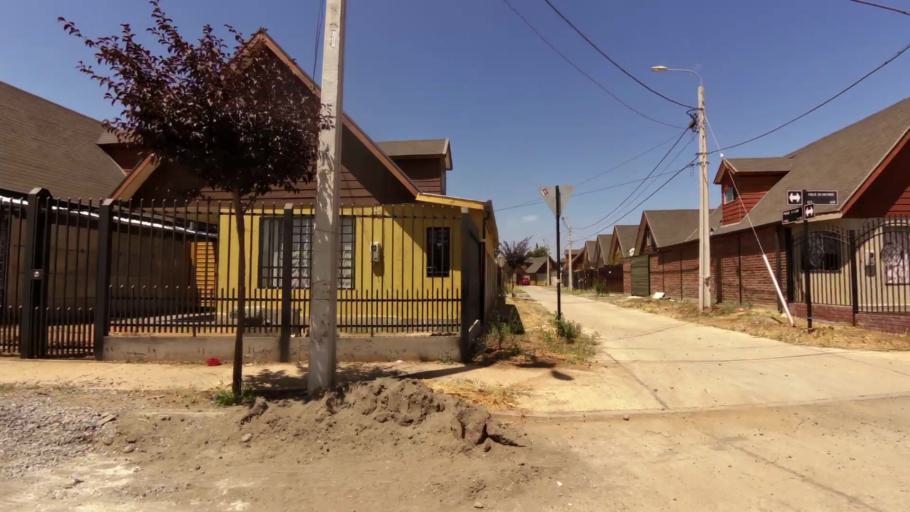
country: CL
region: Maule
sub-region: Provincia de Talca
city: Talca
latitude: -35.4434
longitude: -71.6177
